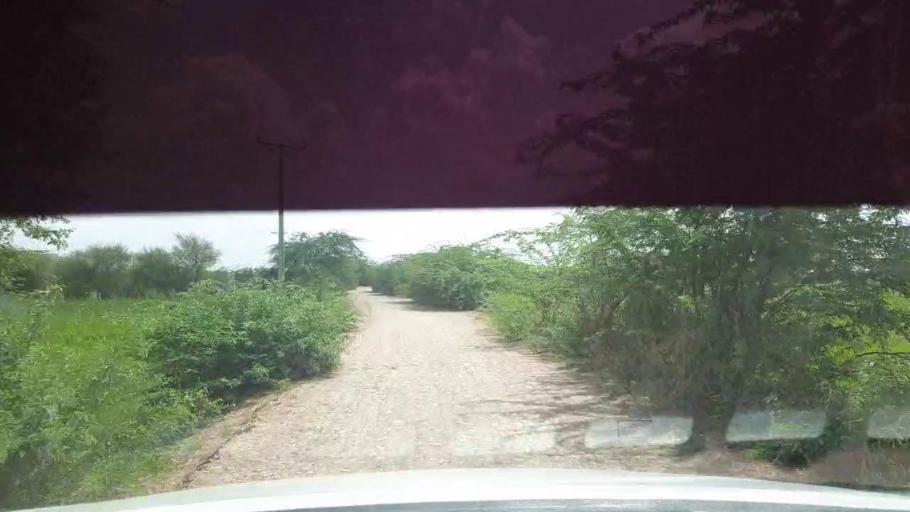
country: PK
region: Sindh
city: Kadhan
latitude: 24.6229
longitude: 69.0332
